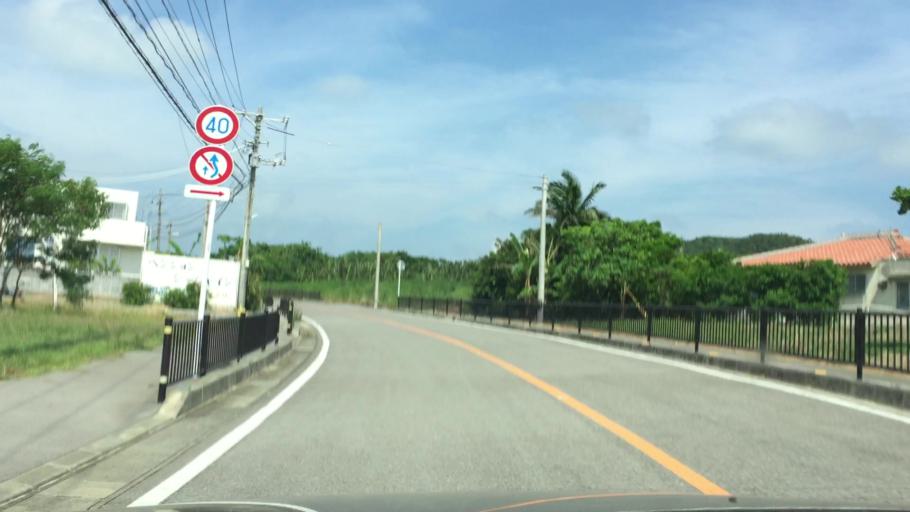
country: JP
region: Okinawa
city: Ishigaki
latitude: 24.4979
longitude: 124.2389
